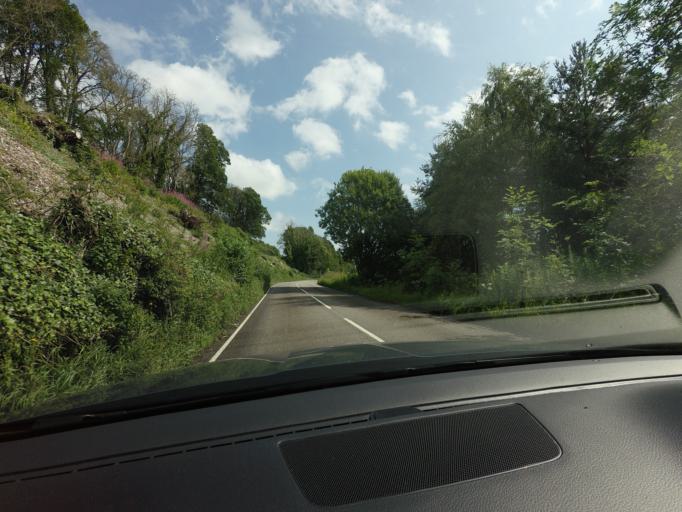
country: GB
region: Scotland
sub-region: Highland
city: Dingwall
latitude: 57.6108
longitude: -4.4074
